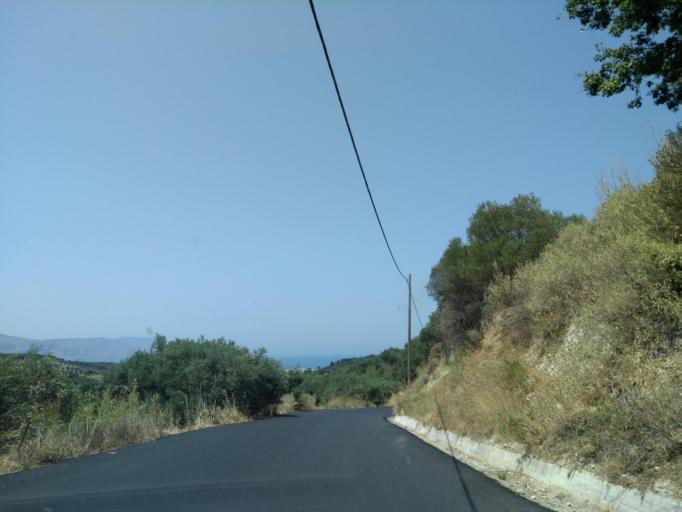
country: GR
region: Crete
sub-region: Nomos Chanias
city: Georgioupolis
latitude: 35.3234
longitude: 24.2999
